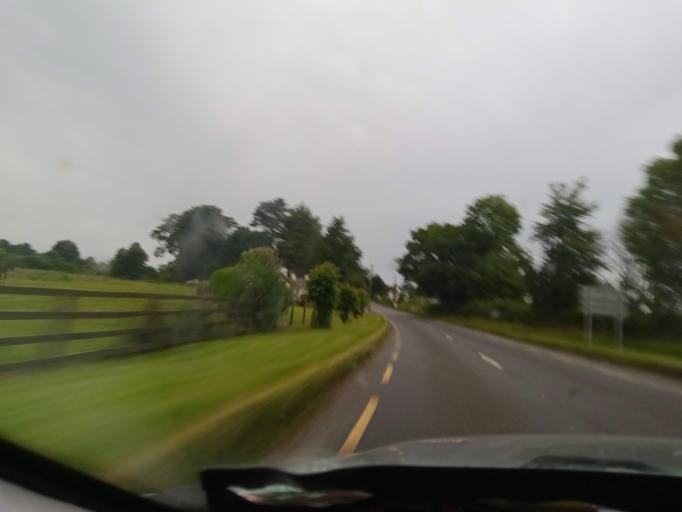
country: IE
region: Leinster
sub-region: Laois
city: Mountmellick
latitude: 53.1334
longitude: -7.3992
